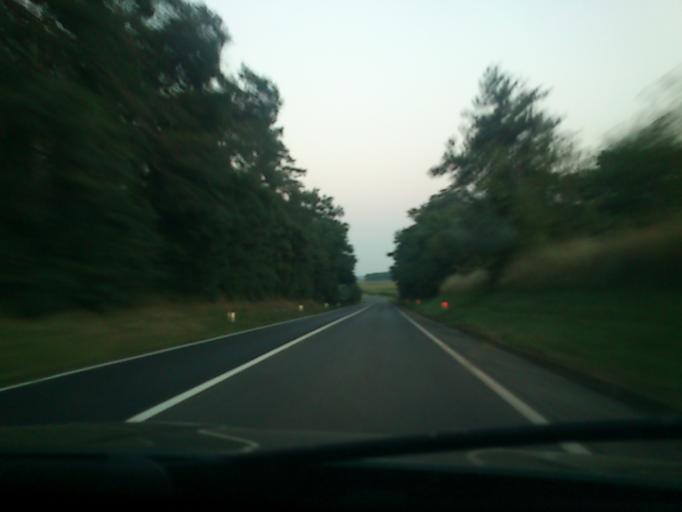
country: SI
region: Duplek
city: Zgornji Duplek
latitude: 46.4946
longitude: 15.7163
